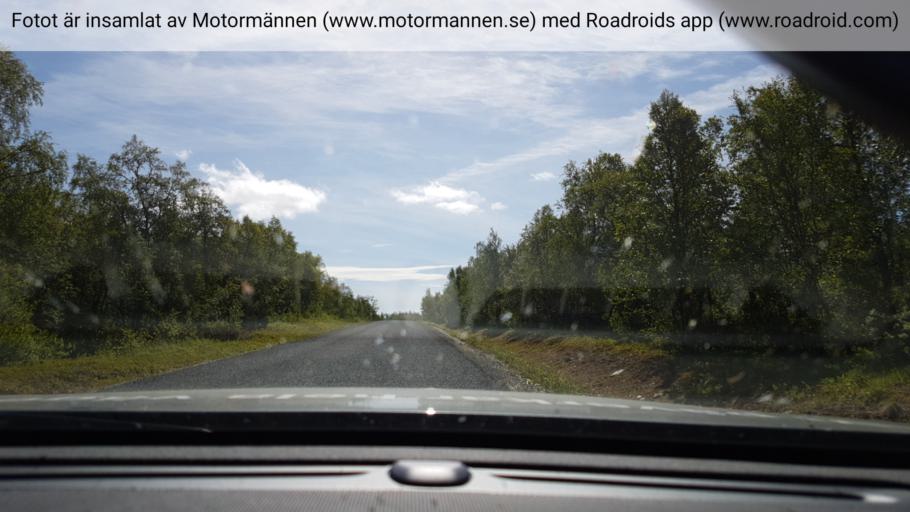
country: NO
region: Nordland
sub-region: Hattfjelldal
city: Hattfjelldal
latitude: 65.4151
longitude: 14.9286
